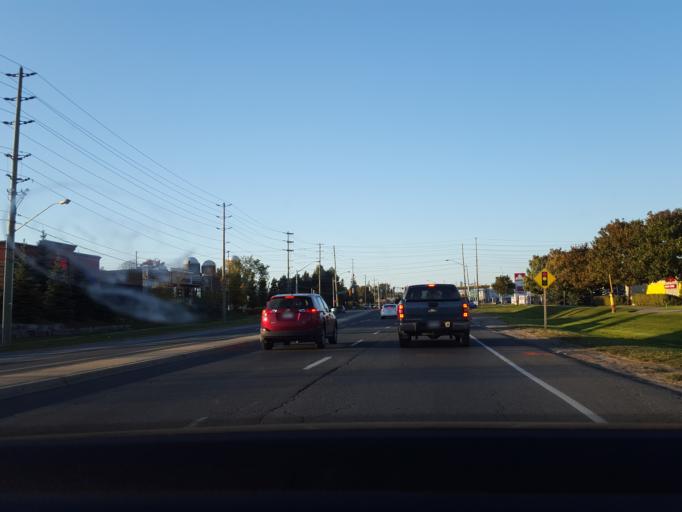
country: CA
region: Ontario
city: Newmarket
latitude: 44.0712
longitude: -79.4843
